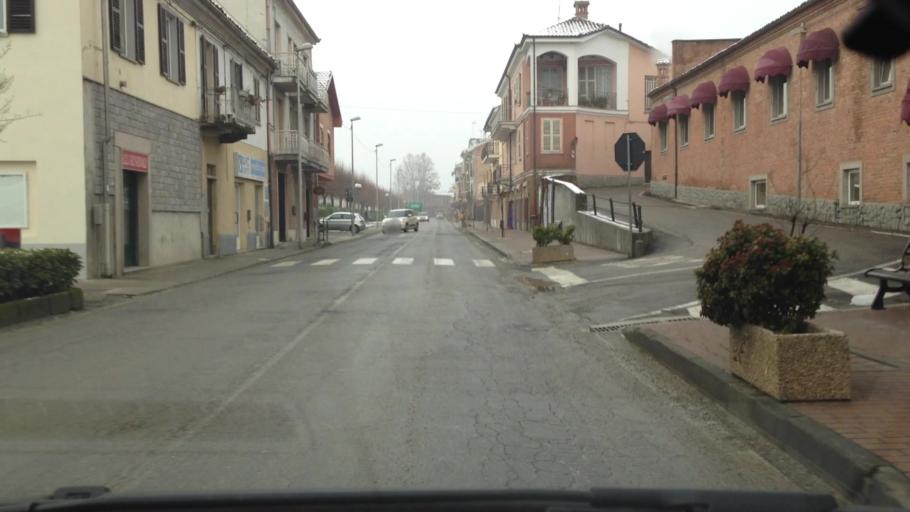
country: IT
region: Piedmont
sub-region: Provincia di Asti
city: Montegrosso
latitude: 44.8191
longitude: 8.2397
